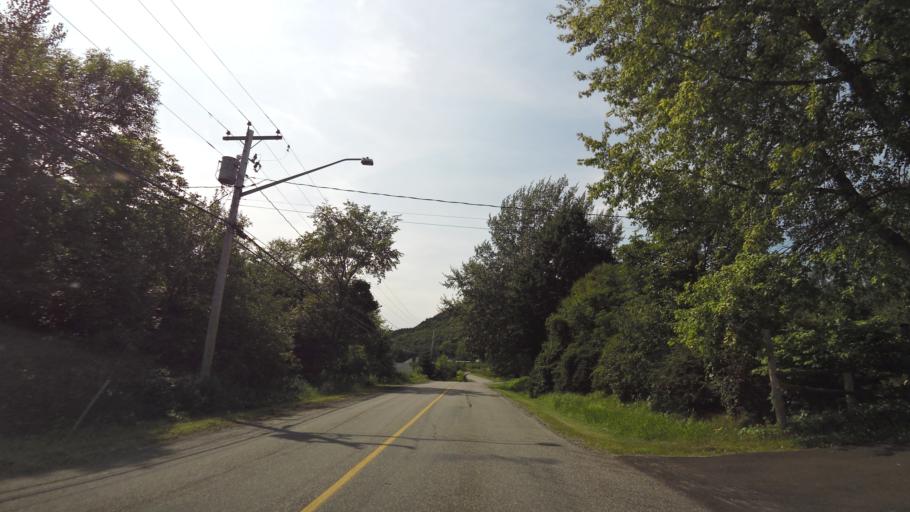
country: CA
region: New Brunswick
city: Hampton
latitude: 45.5384
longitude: -65.8589
